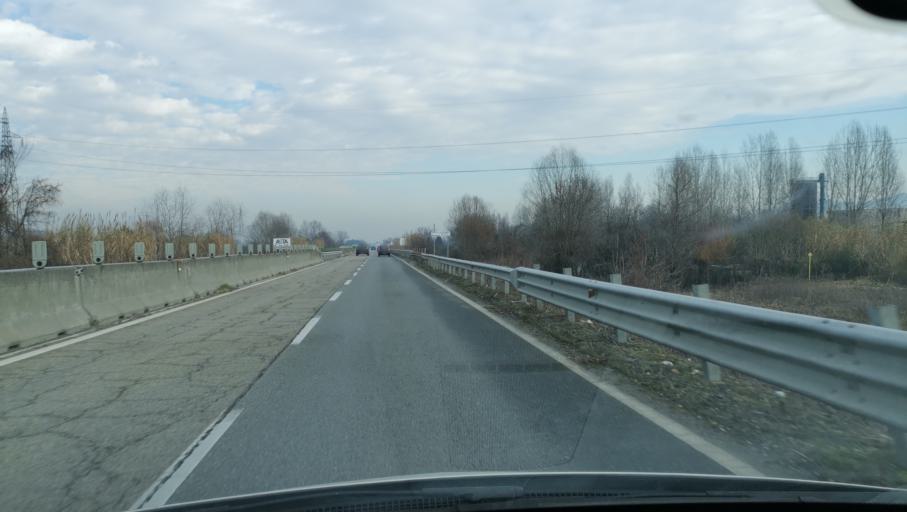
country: IT
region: Piedmont
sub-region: Provincia di Torino
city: Castiglione Torinese
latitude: 45.1378
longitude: 7.7914
